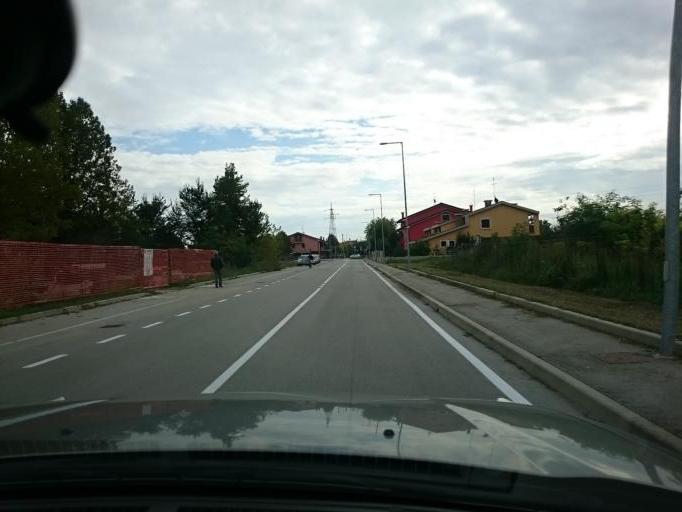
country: IT
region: Veneto
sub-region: Provincia di Padova
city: Ponte San Nicolo
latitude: 45.3771
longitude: 11.9169
